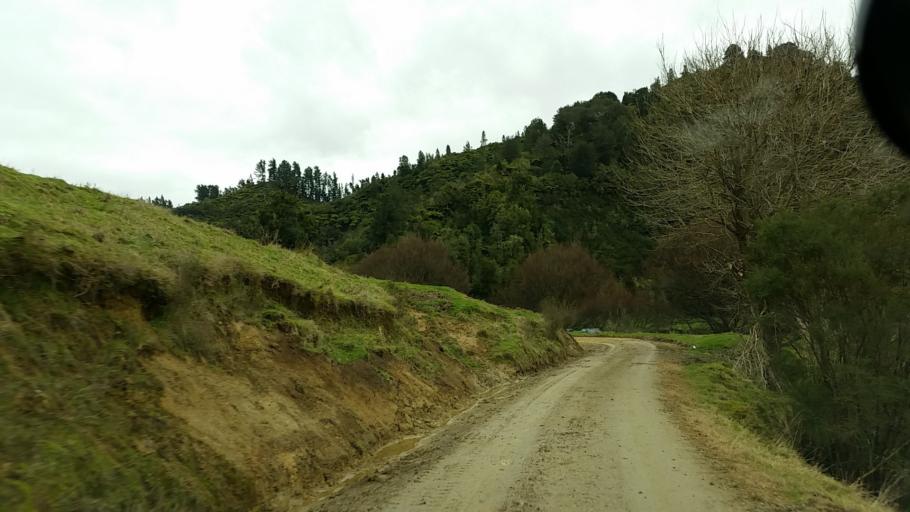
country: NZ
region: Taranaki
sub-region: South Taranaki District
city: Patea
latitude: -39.6589
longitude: 174.7513
